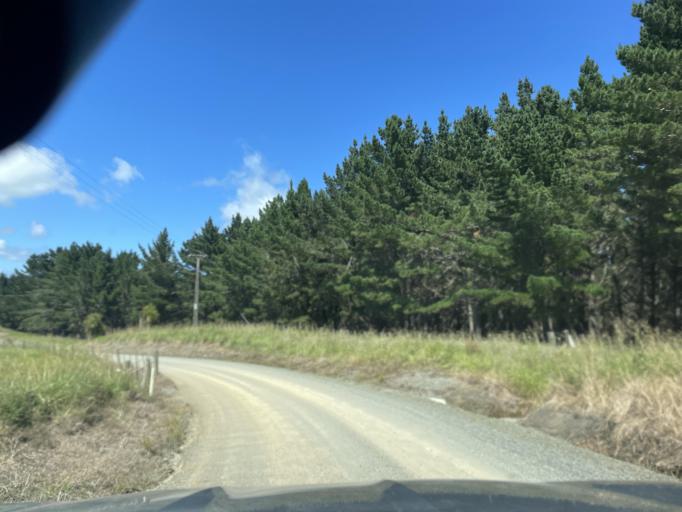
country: NZ
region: Auckland
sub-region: Auckland
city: Wellsford
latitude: -36.2507
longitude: 174.3654
